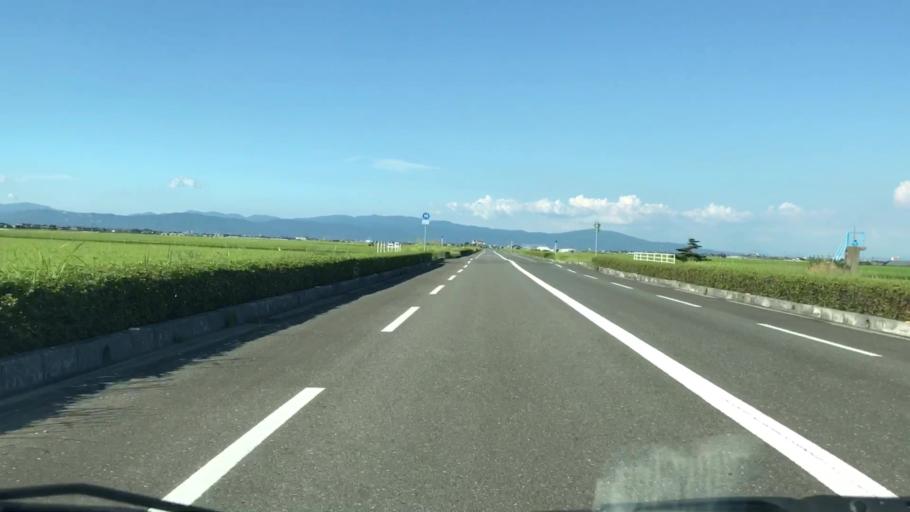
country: JP
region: Saga Prefecture
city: Okawa
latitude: 33.1725
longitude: 130.2954
